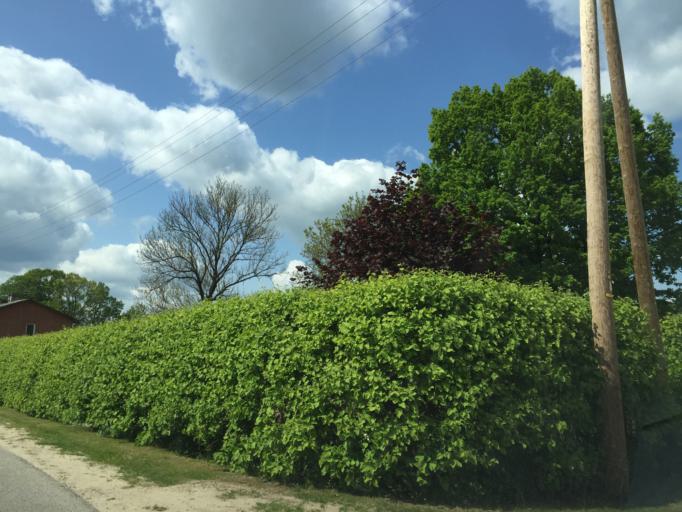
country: LV
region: Baldone
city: Baldone
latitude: 56.7391
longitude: 24.3830
